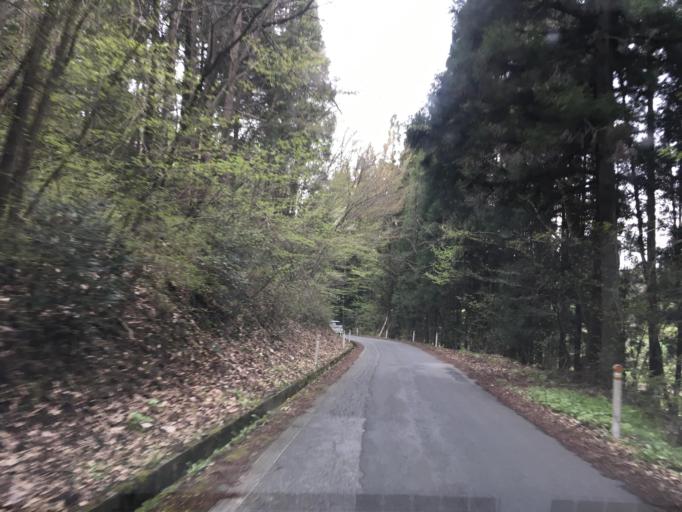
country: JP
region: Iwate
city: Ichinoseki
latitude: 38.8369
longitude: 141.3371
